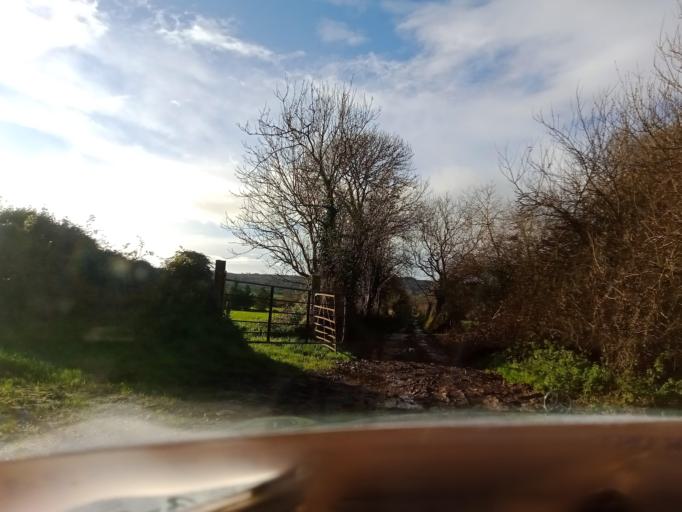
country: IE
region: Leinster
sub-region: Kilkenny
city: Mooncoin
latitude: 52.2759
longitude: -7.2593
